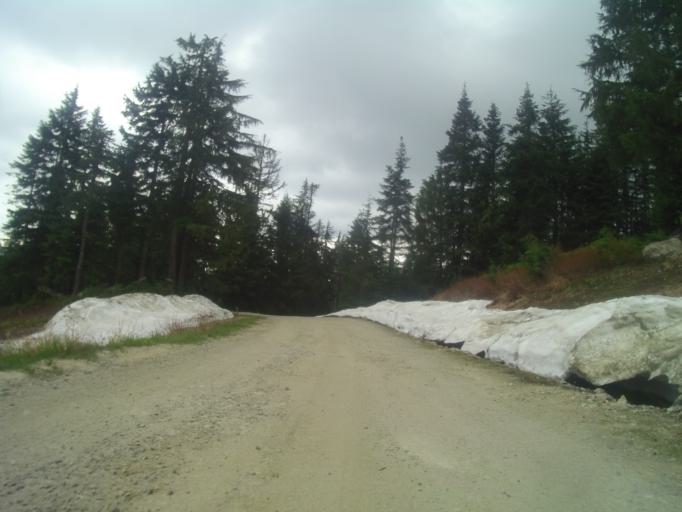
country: CA
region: British Columbia
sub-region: Fraser Valley Regional District
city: North Vancouver
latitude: 49.3784
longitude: -123.0745
